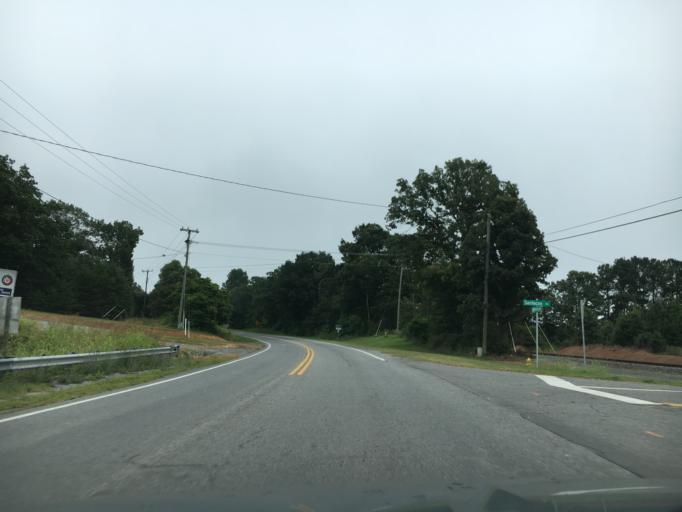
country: US
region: Virginia
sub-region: Campbell County
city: Brookneal
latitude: 37.0620
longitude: -78.9636
